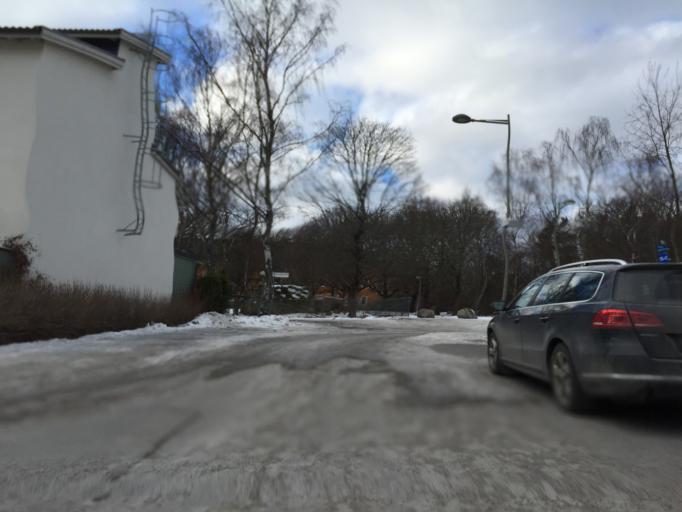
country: SE
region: Stockholm
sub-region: Stockholms Kommun
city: Bromma
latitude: 59.3570
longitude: 17.9053
